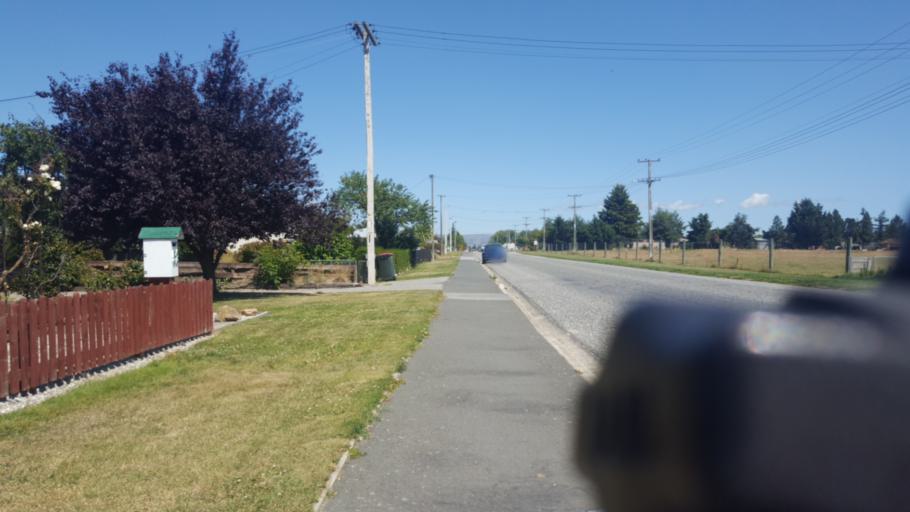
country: NZ
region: Otago
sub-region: Dunedin City
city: Dunedin
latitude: -45.1257
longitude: 170.1043
